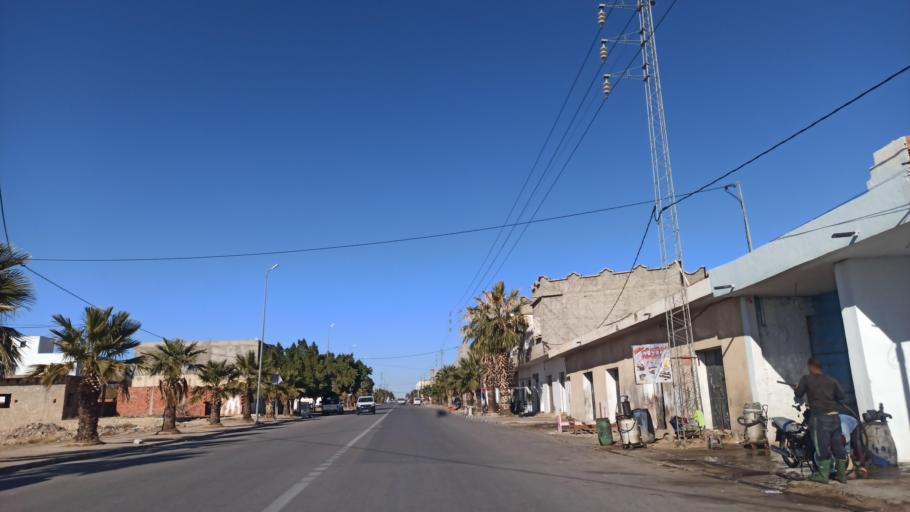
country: TN
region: Sidi Bu Zayd
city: Jilma
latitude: 35.2753
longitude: 9.4190
